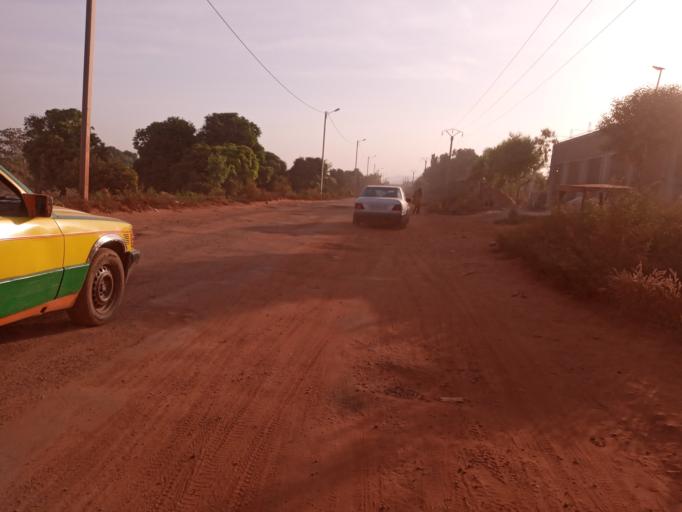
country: ML
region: Bamako
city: Bamako
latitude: 12.6352
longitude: -7.9318
